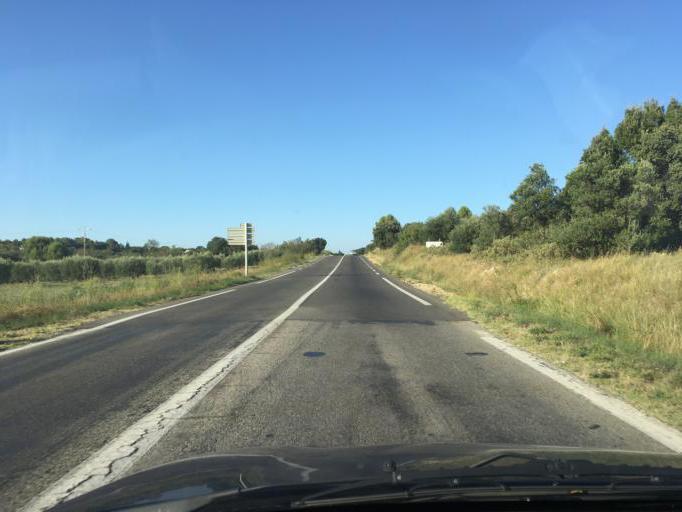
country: FR
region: Languedoc-Roussillon
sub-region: Departement du Gard
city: Ledenon
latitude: 43.9046
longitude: 4.5202
